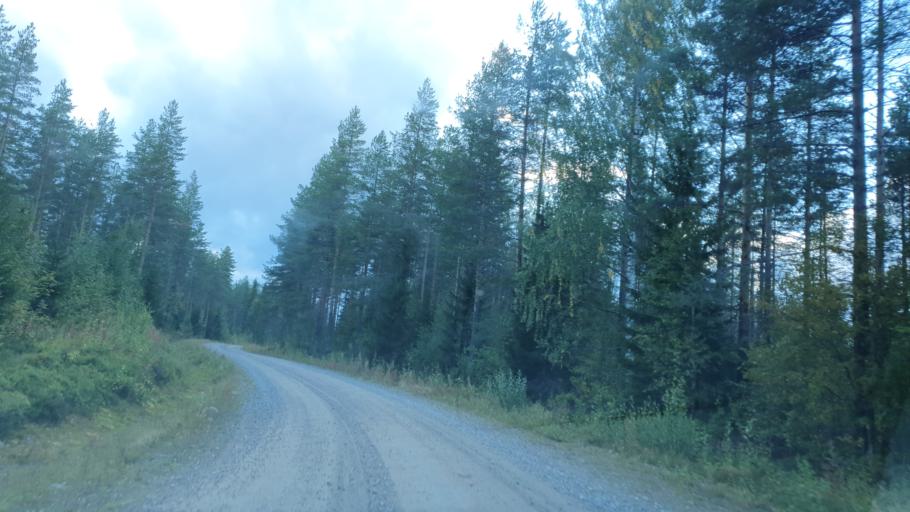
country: FI
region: Kainuu
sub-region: Kehys-Kainuu
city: Kuhmo
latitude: 64.3365
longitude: 29.9170
